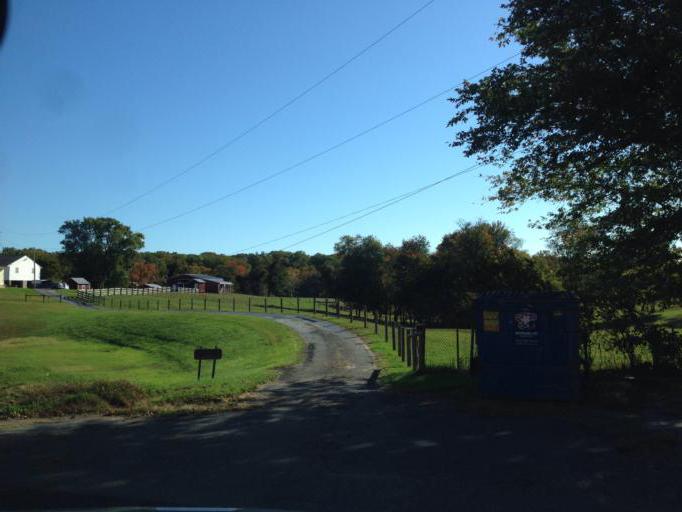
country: US
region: Maryland
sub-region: Howard County
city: Fulton
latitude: 39.1357
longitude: -76.9083
